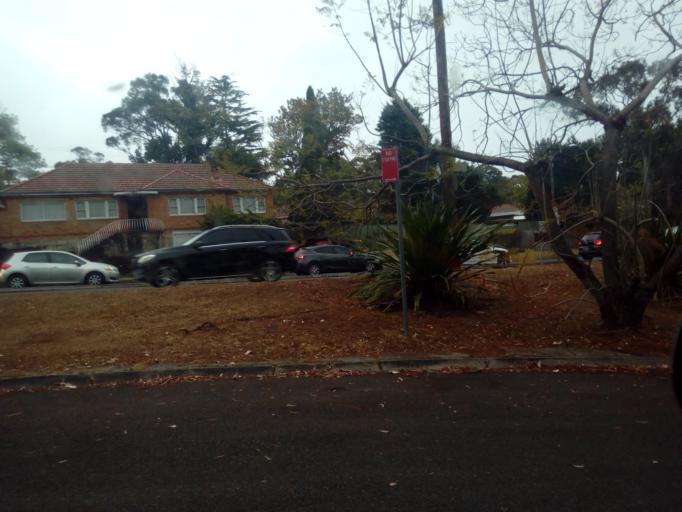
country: AU
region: New South Wales
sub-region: Ku-ring-gai
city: Roseville Chase
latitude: -33.7824
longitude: 151.1951
